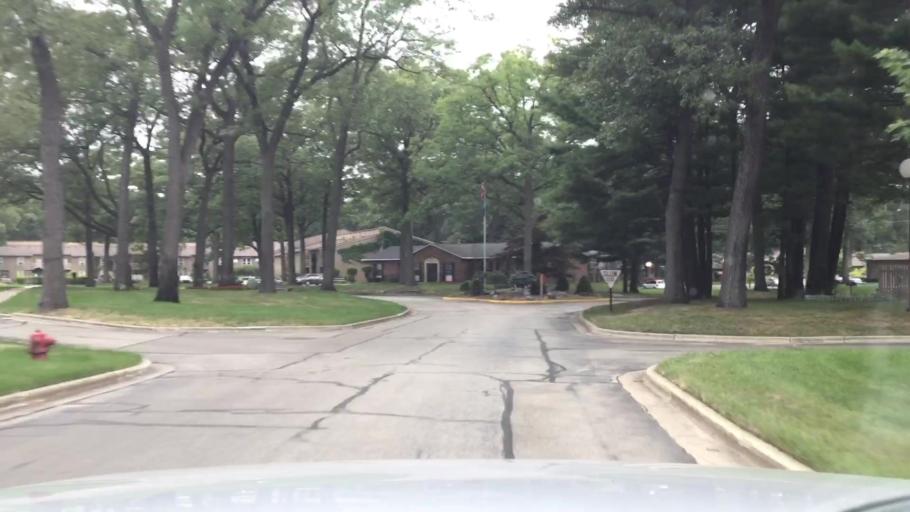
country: US
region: Michigan
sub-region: Muskegon County
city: Muskegon
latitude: 43.2397
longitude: -86.1948
